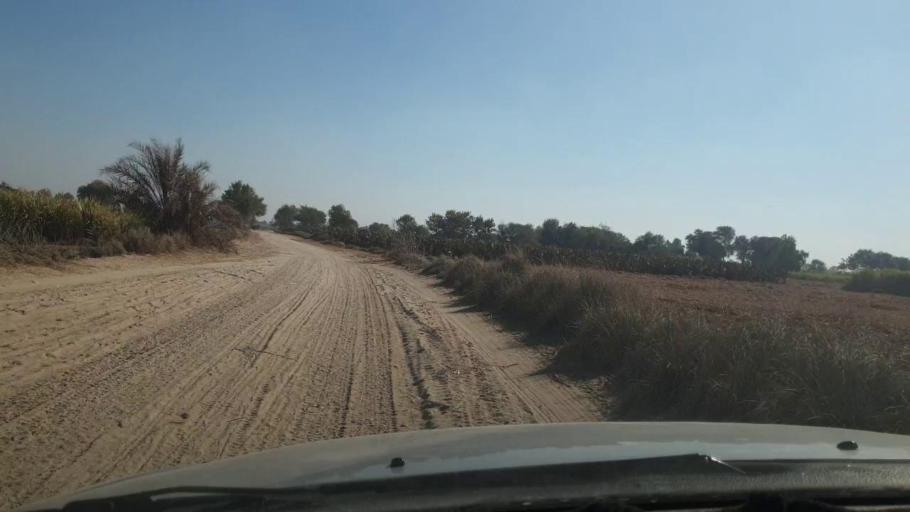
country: PK
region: Sindh
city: Ghotki
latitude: 28.0237
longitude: 69.2203
